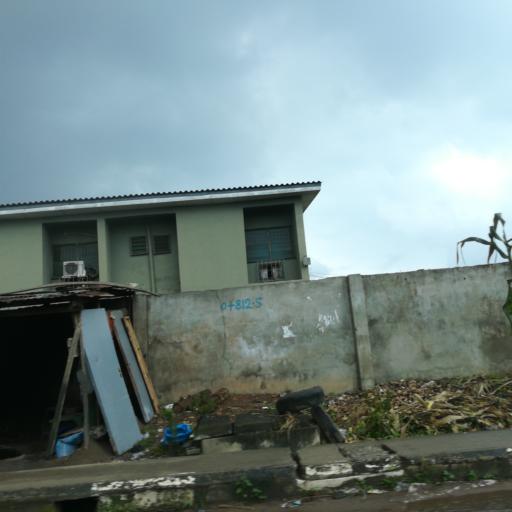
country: NG
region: Lagos
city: Agege
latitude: 6.5921
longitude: 3.2945
